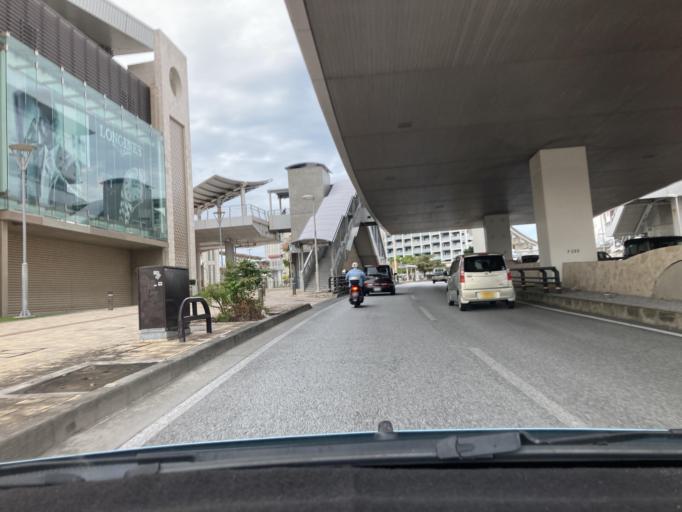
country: JP
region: Okinawa
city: Naha-shi
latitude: 26.2226
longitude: 127.6984
